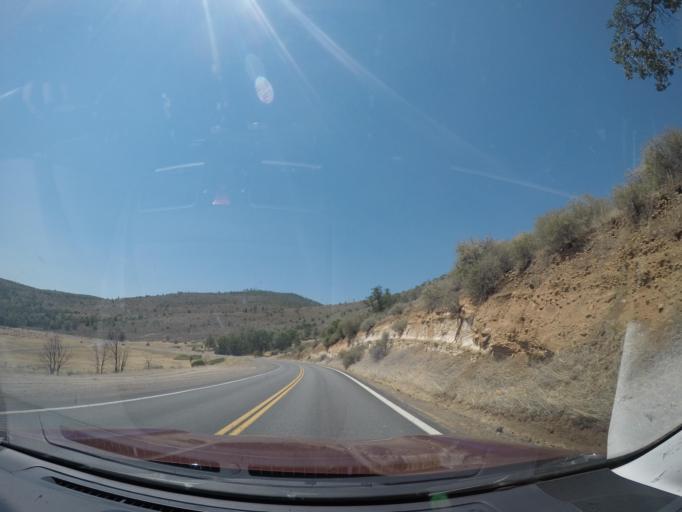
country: US
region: California
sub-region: Shasta County
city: Burney
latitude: 41.0012
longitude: -121.5022
